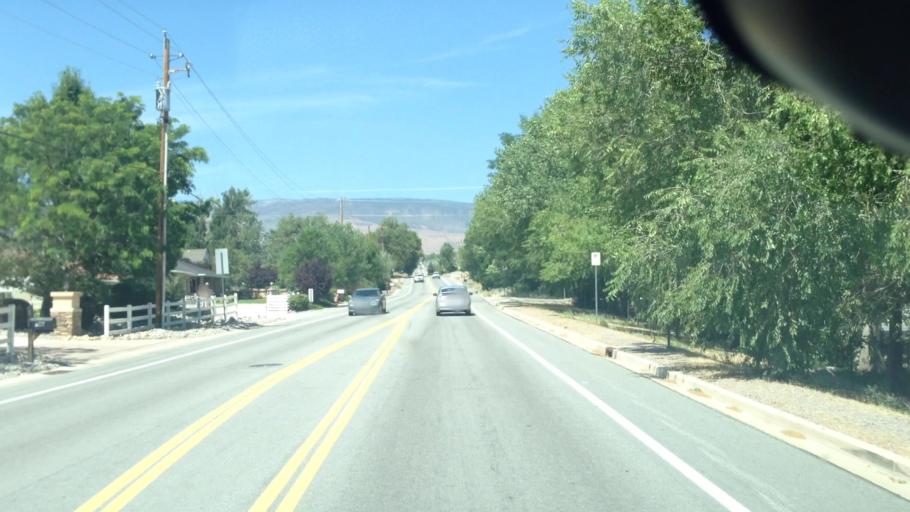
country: US
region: Nevada
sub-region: Washoe County
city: Sparks
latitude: 39.4186
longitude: -119.7642
